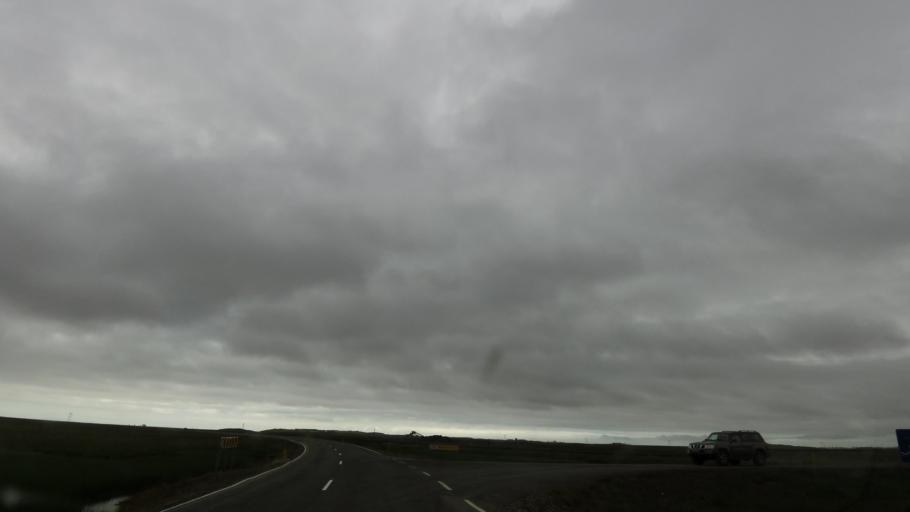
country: IS
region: East
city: Hoefn
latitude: 64.3168
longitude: -15.4141
